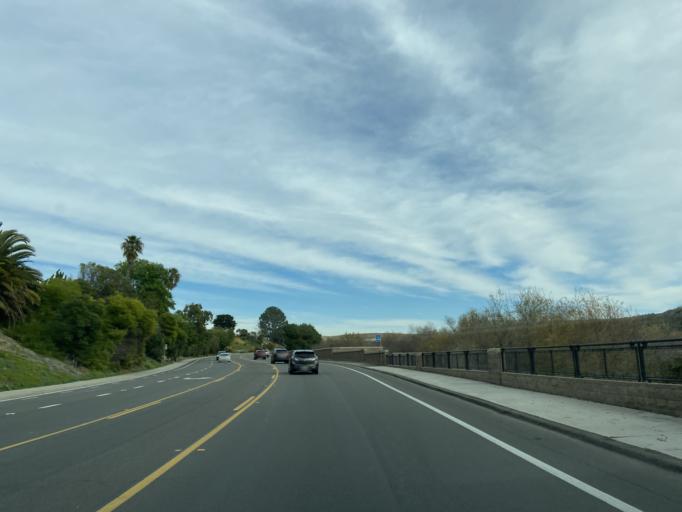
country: US
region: California
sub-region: San Diego County
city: Oceanside
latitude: 33.2086
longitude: -117.3324
